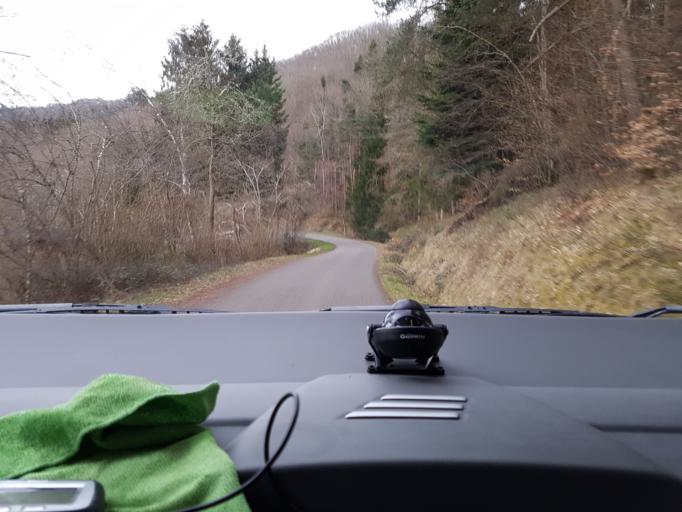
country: FR
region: Auvergne
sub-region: Departement du Puy-de-Dome
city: Chapdes-Beaufort
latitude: 45.8614
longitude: 2.8363
